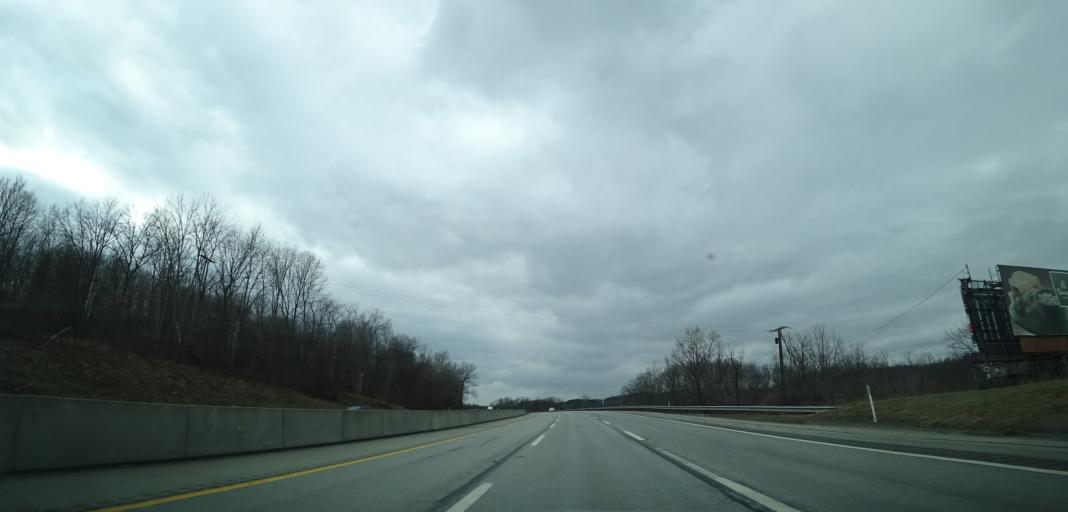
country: US
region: Pennsylvania
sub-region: Lawrence County
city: New Beaver
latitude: 40.8846
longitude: -80.4280
